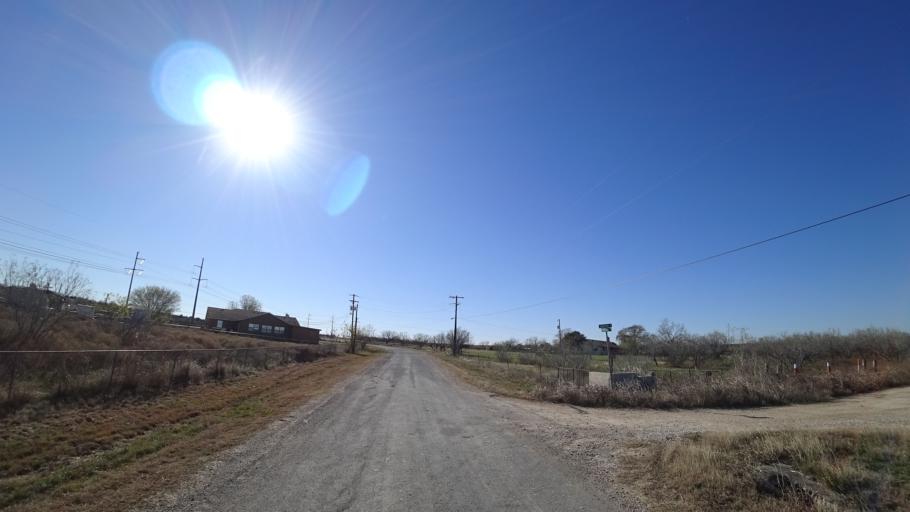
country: US
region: Texas
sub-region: Travis County
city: Onion Creek
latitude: 30.1060
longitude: -97.6770
